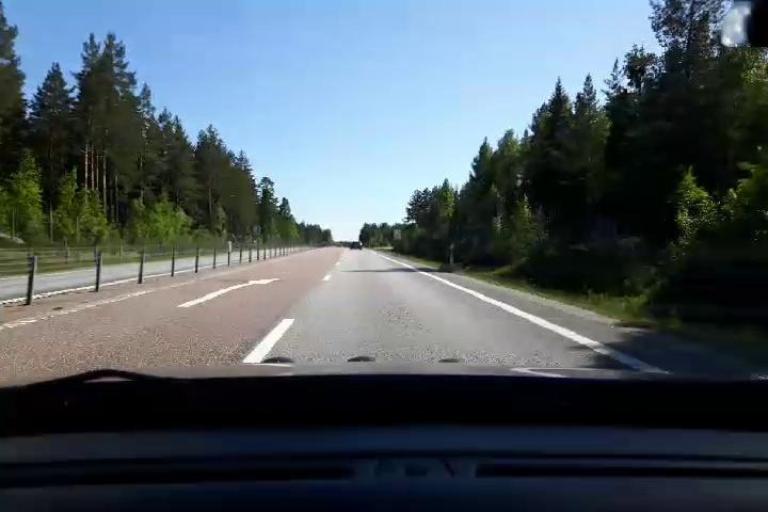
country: SE
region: Gaevleborg
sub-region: Soderhamns Kommun
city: Ljusne
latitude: 61.1262
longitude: 17.0150
